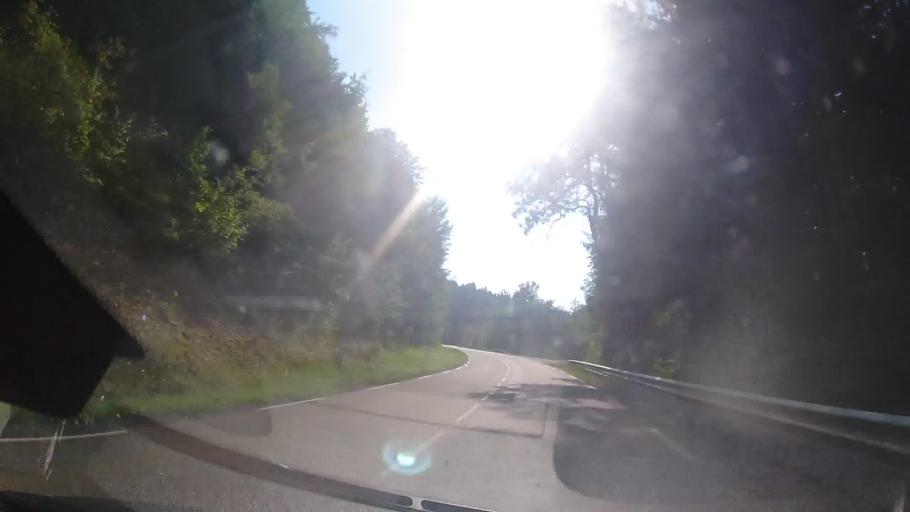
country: FR
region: Franche-Comte
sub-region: Departement du Jura
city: Clairvaux-les-Lacs
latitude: 46.5850
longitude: 5.8222
